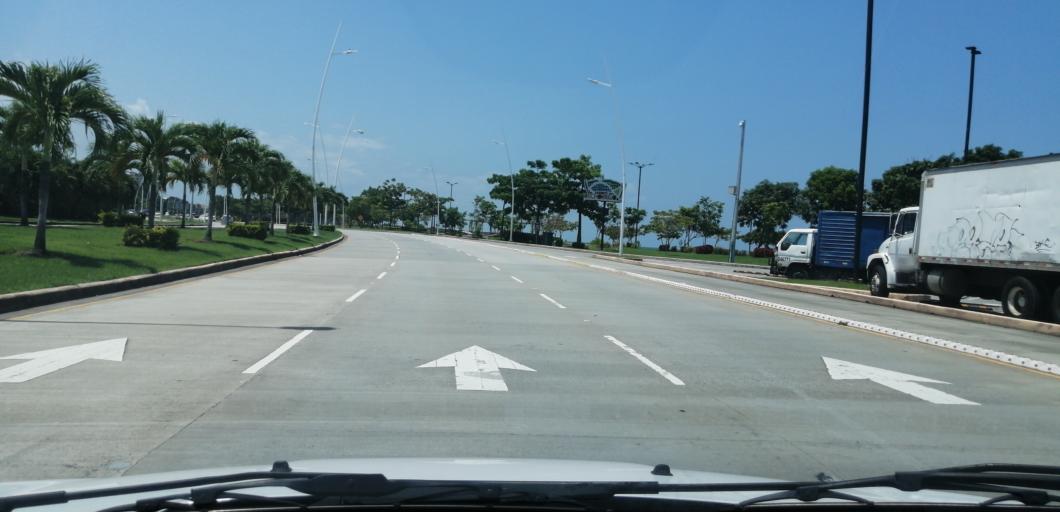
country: PA
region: Panama
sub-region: Distrito de Panama
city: Ancon
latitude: 8.9466
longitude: -79.5486
